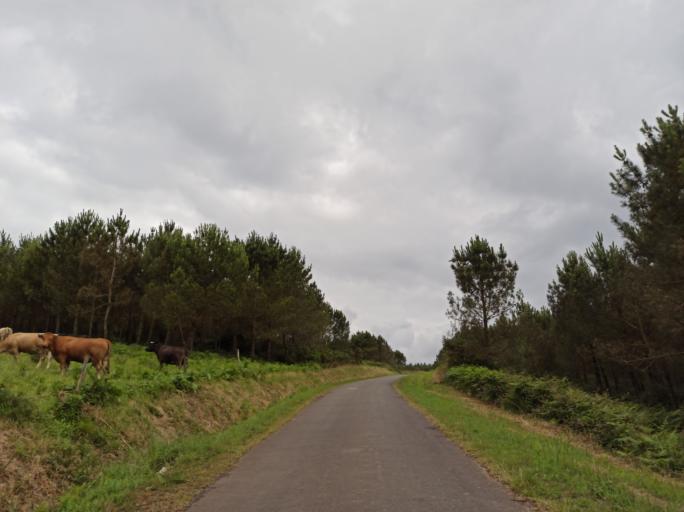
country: ES
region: Galicia
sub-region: Provincia de Pontevedra
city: Silleda
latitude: 42.7682
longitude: -8.1622
